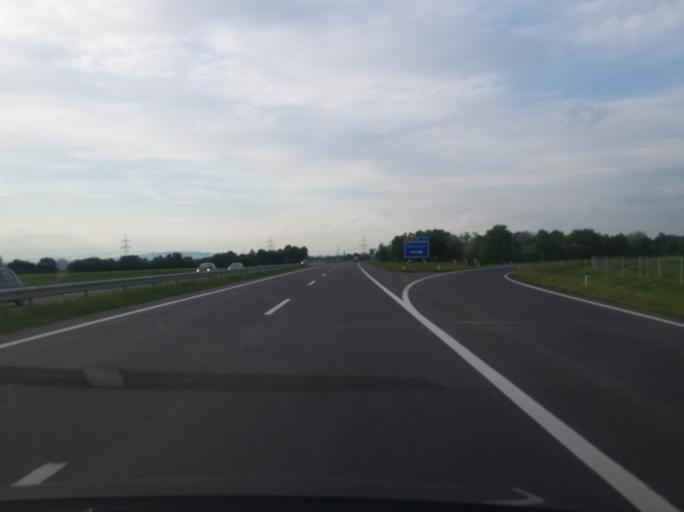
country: AT
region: Burgenland
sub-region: Eisenstadt-Umgebung
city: Hornstein
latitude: 47.8639
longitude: 16.4203
